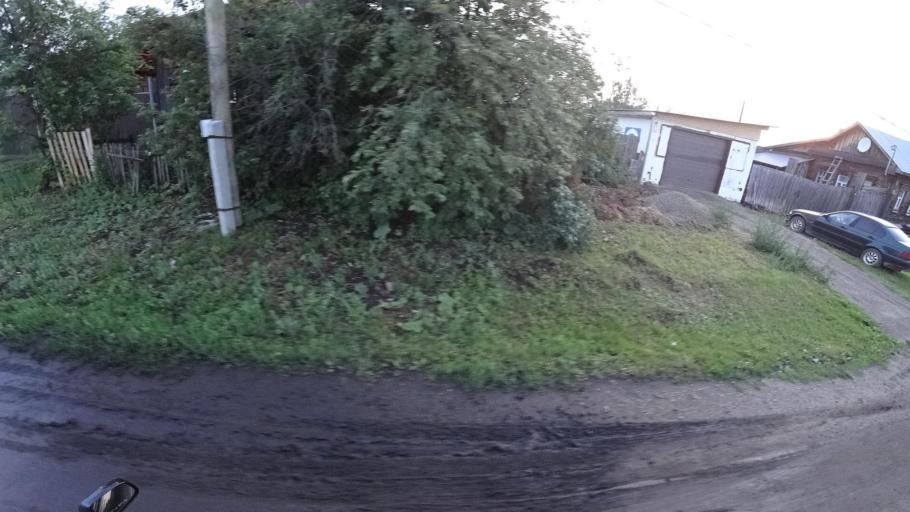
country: RU
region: Sverdlovsk
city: Kamyshlov
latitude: 56.8589
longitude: 62.7139
